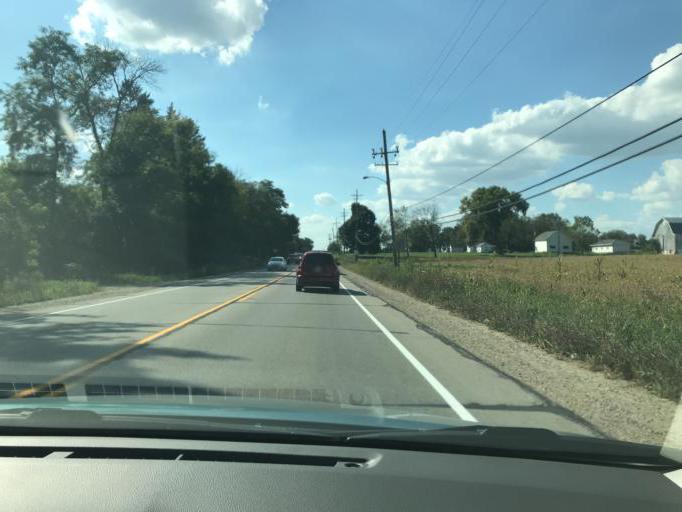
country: US
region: Wisconsin
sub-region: Walworth County
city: Delavan
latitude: 42.6280
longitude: -88.5942
